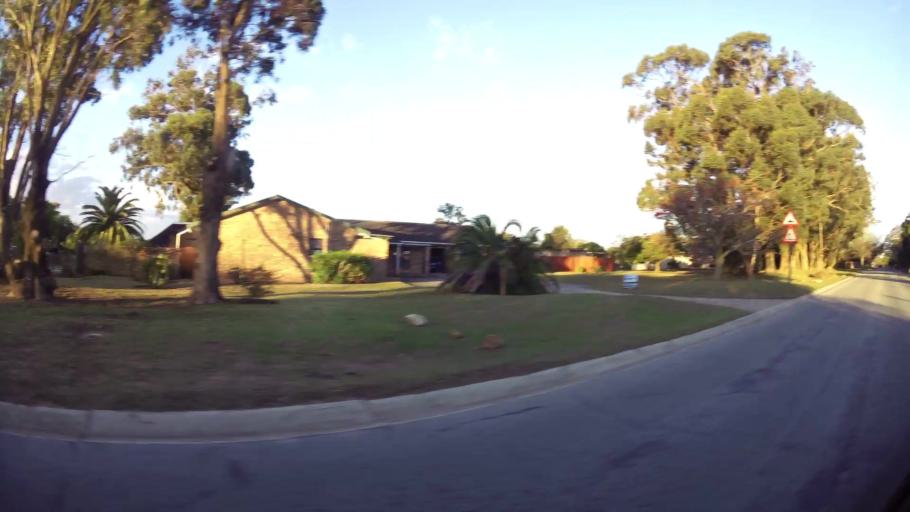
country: ZA
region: Eastern Cape
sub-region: Nelson Mandela Bay Metropolitan Municipality
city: Port Elizabeth
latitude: -33.9708
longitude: 25.5211
